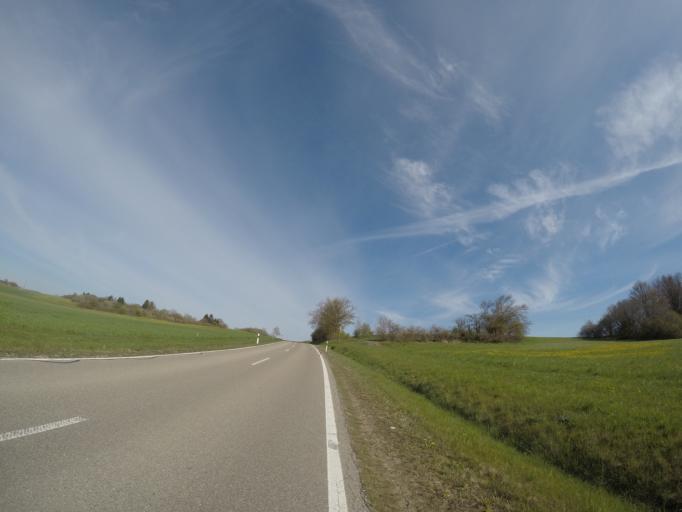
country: DE
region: Baden-Wuerttemberg
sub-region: Tuebingen Region
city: Laichingen
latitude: 48.4988
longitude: 9.6779
